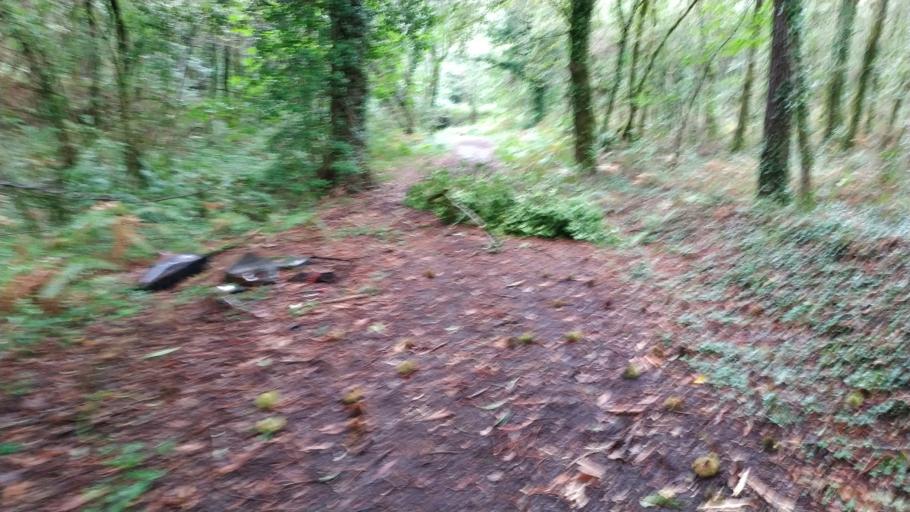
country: ES
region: Galicia
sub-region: Provincia da Coruna
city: Negreira
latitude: 42.9126
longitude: -8.7504
